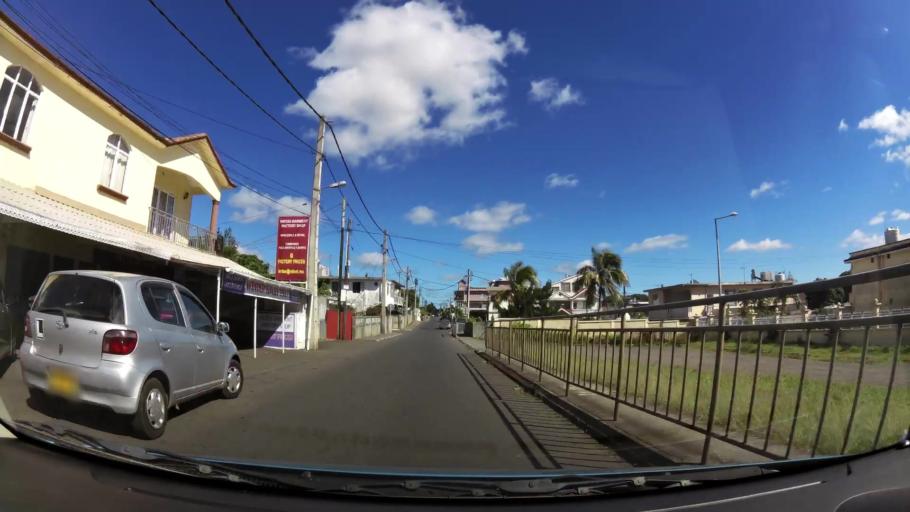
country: MU
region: Plaines Wilhems
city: Vacoas
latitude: -20.2861
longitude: 57.4791
